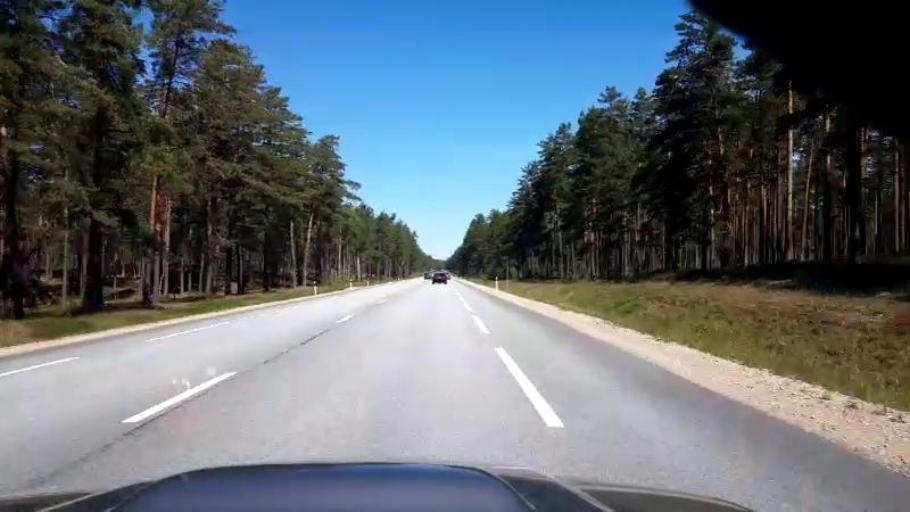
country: LV
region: Carnikava
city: Carnikava
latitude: 57.1674
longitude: 24.3444
